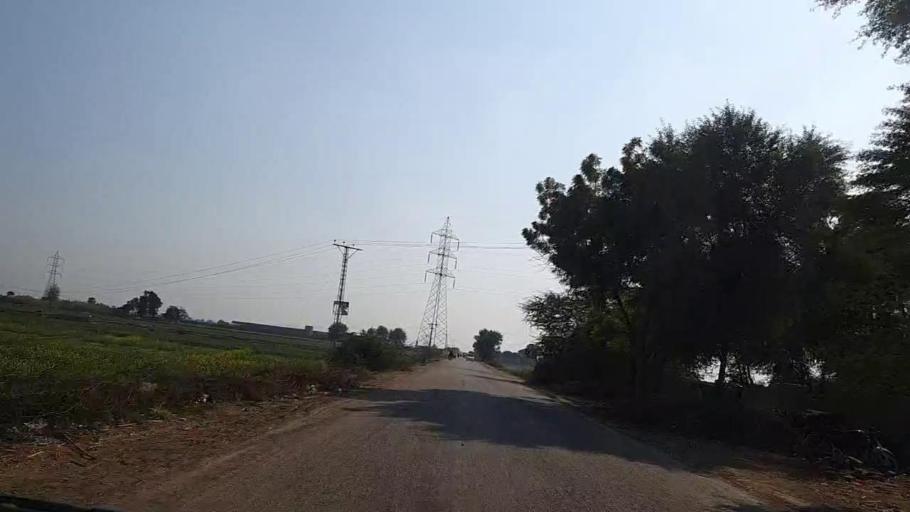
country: PK
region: Sindh
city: Sakrand
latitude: 26.1089
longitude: 68.2909
